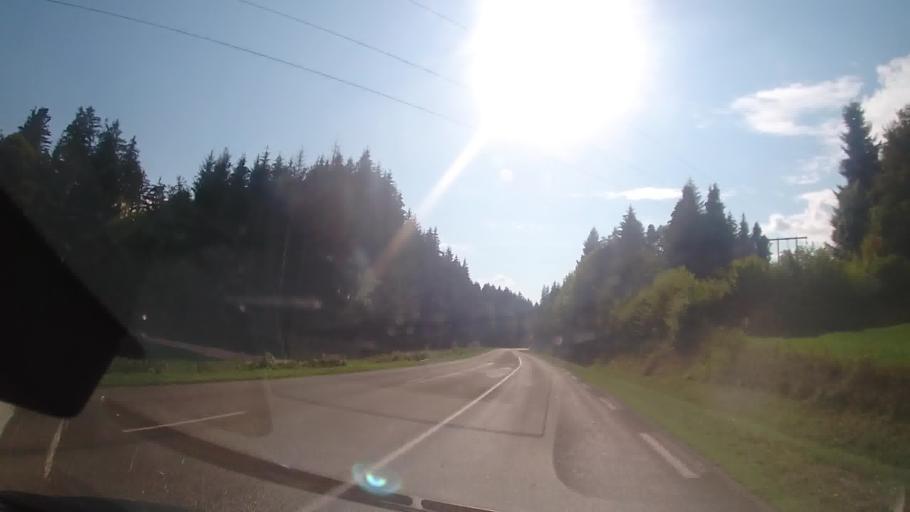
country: FR
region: Franche-Comte
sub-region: Departement du Jura
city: Clairvaux-les-Lacs
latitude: 46.5820
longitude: 5.7875
